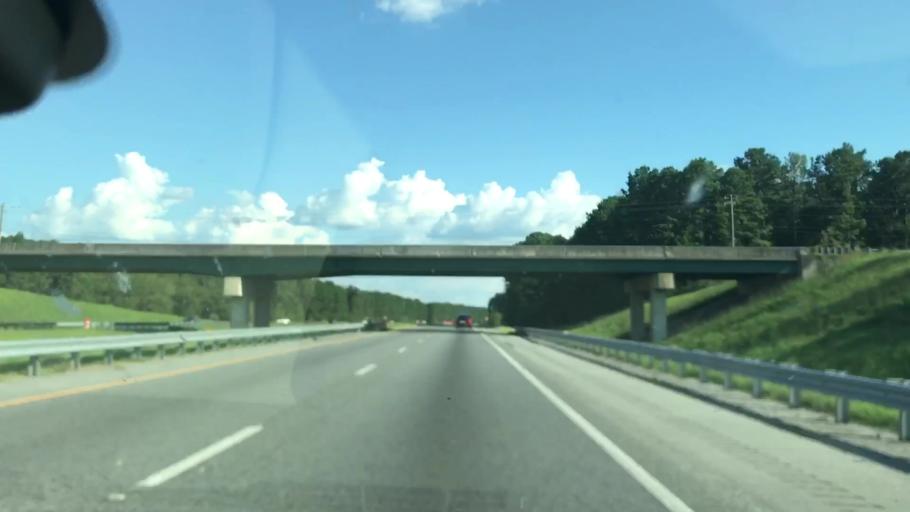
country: US
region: Georgia
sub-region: Harris County
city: Hamilton
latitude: 32.6630
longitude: -84.9813
